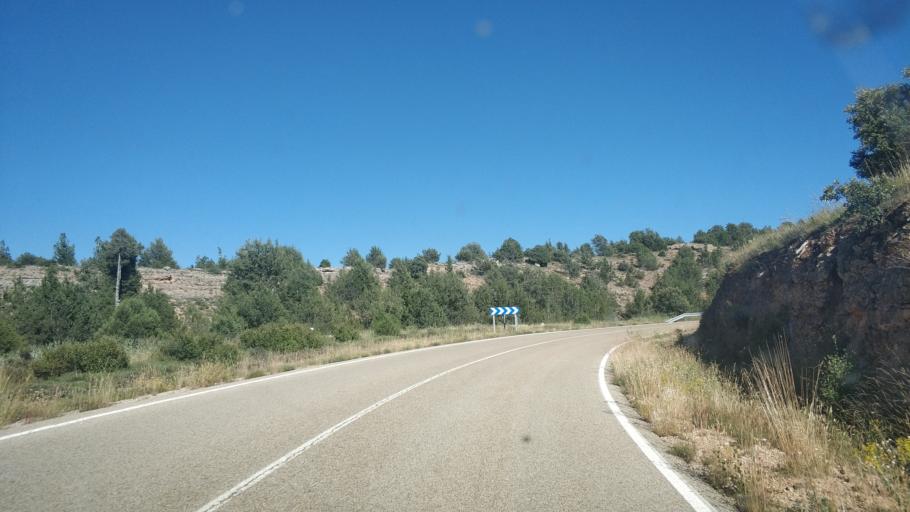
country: ES
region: Castille and Leon
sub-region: Provincia de Soria
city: Montejo de Tiermes
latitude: 41.4297
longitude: -3.2036
